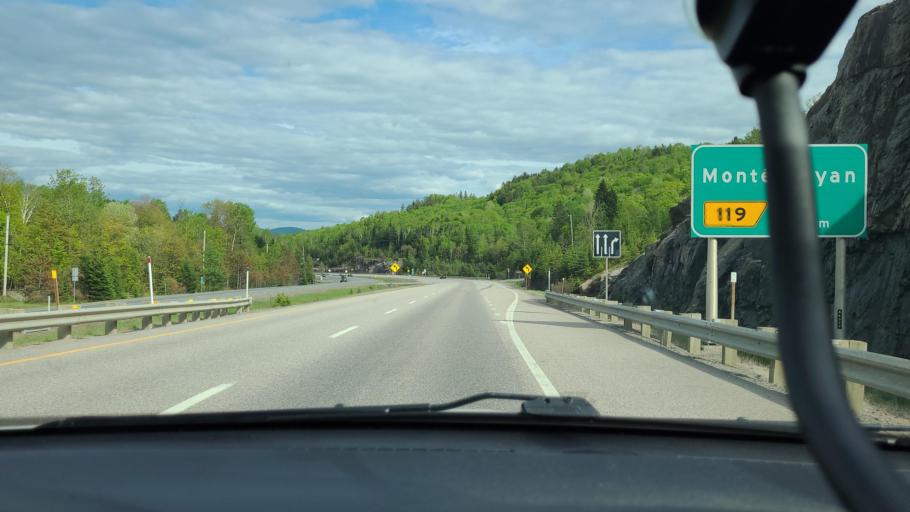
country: CA
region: Quebec
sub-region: Laurentides
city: Mont-Tremblant
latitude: 46.1372
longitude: -74.6319
